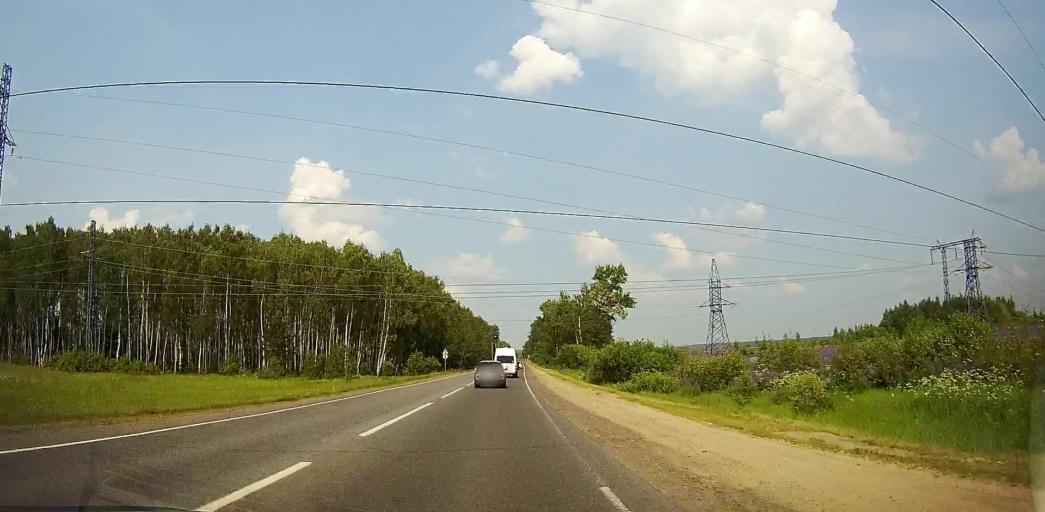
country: RU
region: Moskovskaya
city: Stupino
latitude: 54.9272
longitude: 38.1187
